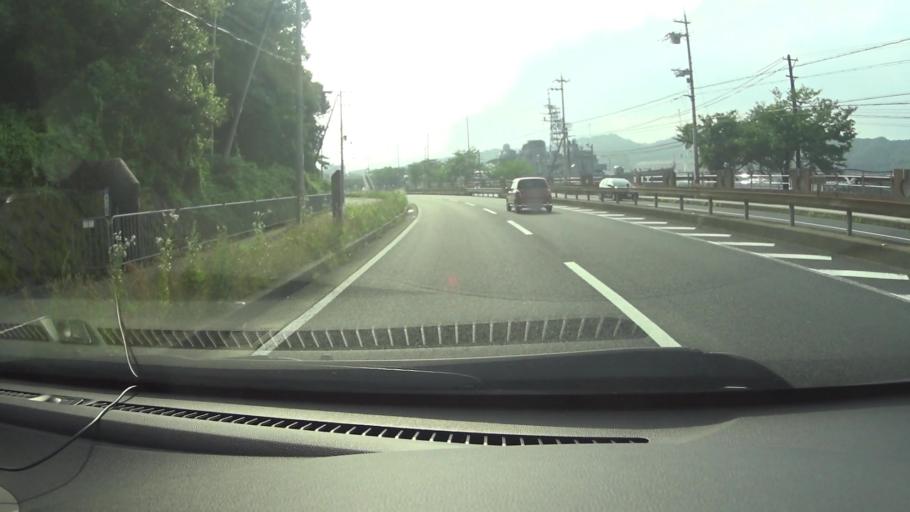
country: JP
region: Kyoto
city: Maizuru
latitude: 35.4761
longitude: 135.3780
